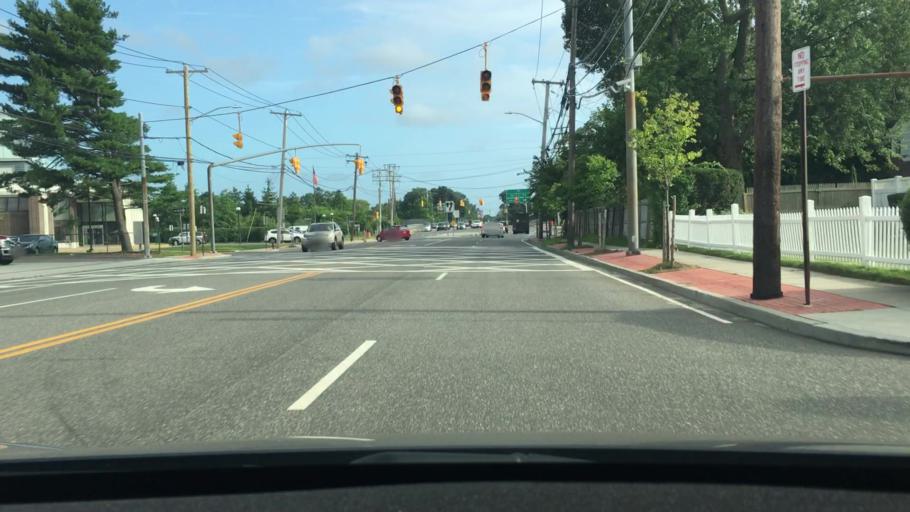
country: US
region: New York
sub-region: Nassau County
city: Syosset
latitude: 40.7997
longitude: -73.5028
